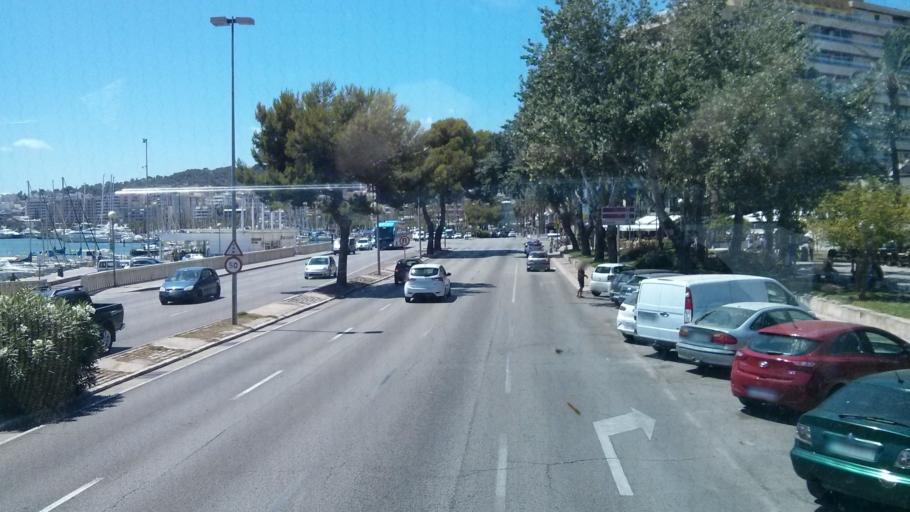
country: ES
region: Balearic Islands
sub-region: Illes Balears
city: Palma
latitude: 39.5690
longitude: 2.6362
